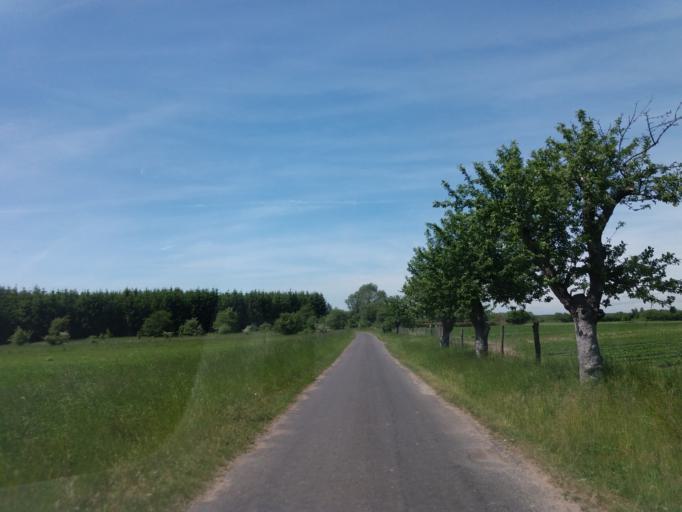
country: PL
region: West Pomeranian Voivodeship
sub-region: Powiat stargardzki
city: Dobrzany
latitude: 53.3522
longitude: 15.4417
